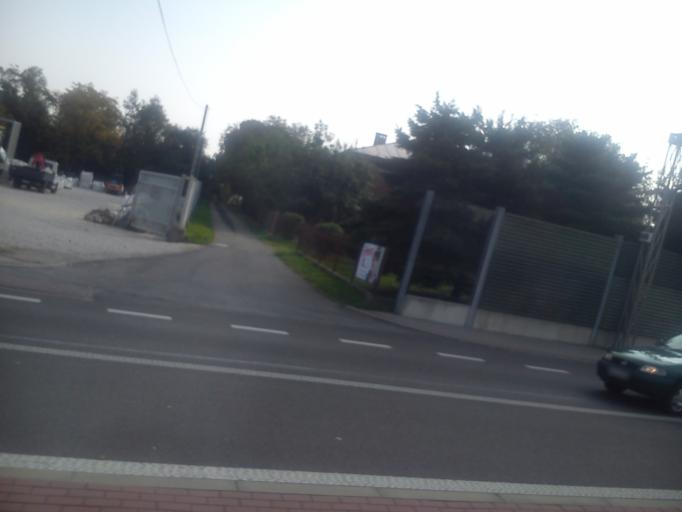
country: PL
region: Subcarpathian Voivodeship
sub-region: Powiat lancucki
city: Lancut
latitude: 50.0581
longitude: 22.2095
